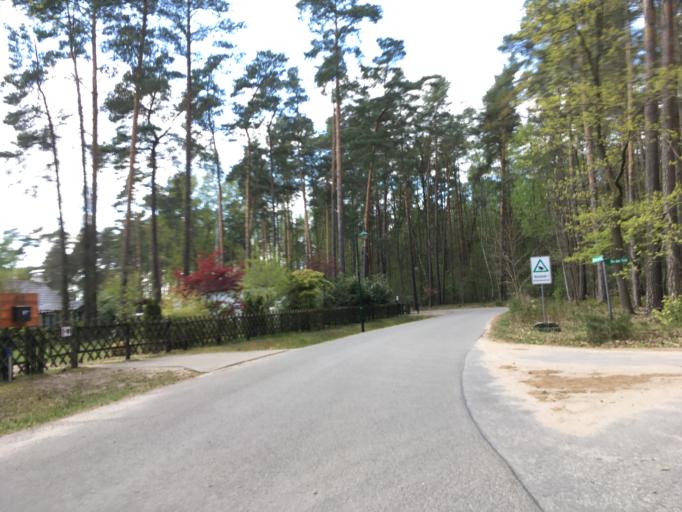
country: DE
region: Brandenburg
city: Wandlitz
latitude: 52.7622
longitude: 13.4418
